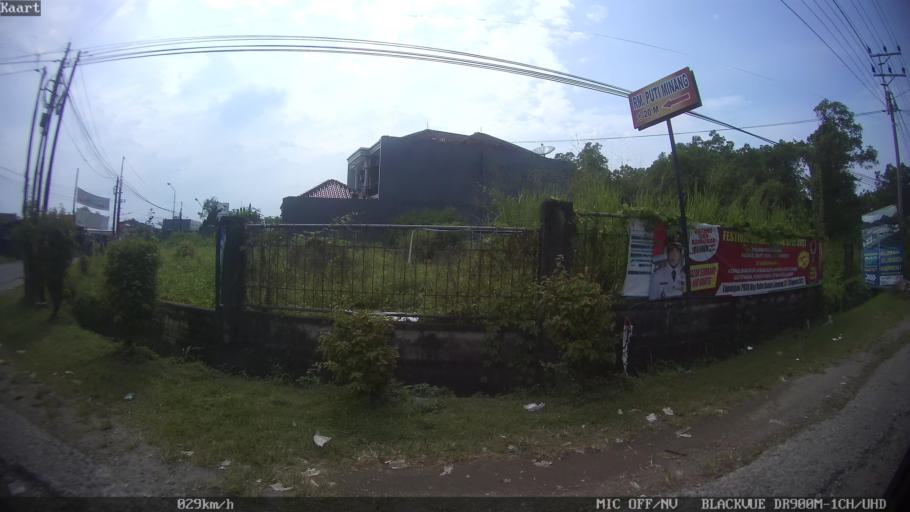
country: ID
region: Lampung
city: Bandarlampung
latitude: -5.4648
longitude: 105.2439
